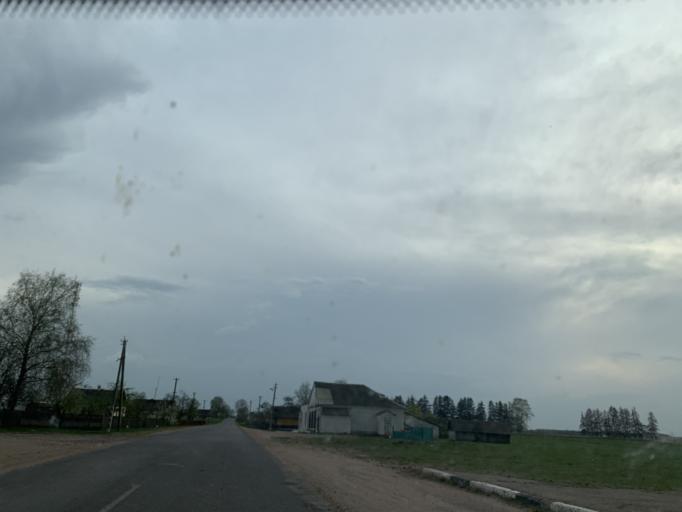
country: BY
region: Minsk
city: Kapyl'
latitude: 53.2797
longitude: 26.9759
